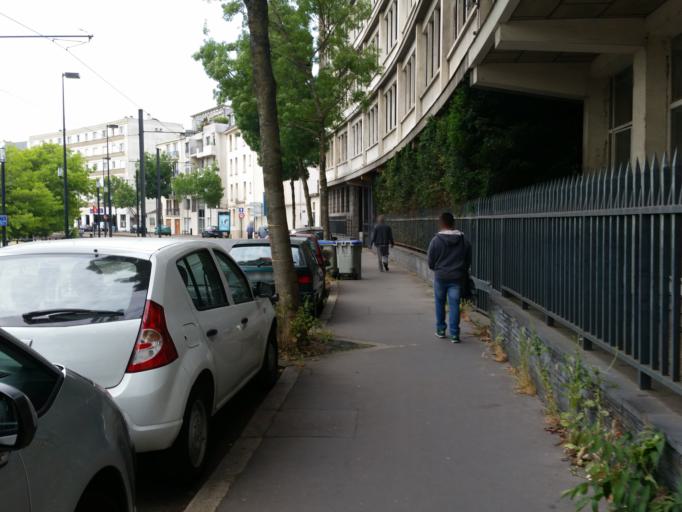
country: FR
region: Pays de la Loire
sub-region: Departement de la Loire-Atlantique
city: Nantes
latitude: 47.2267
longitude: -1.5557
